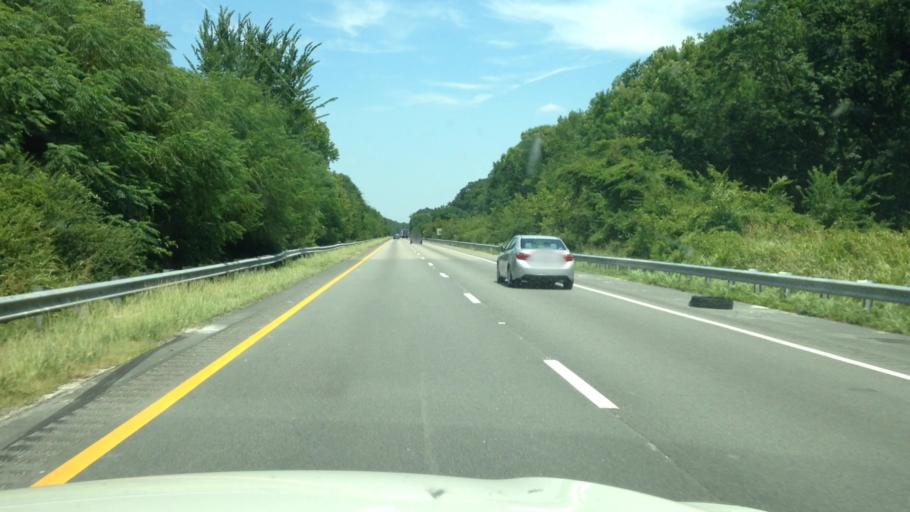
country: US
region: South Carolina
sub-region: Florence County
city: Florence
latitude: 34.3018
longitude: -79.6294
